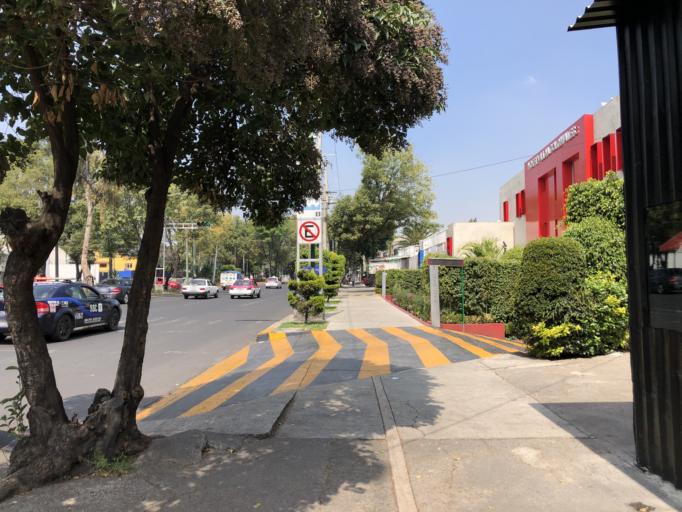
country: MX
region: Mexico City
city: Azcapotzalco
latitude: 19.4742
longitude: -99.1814
